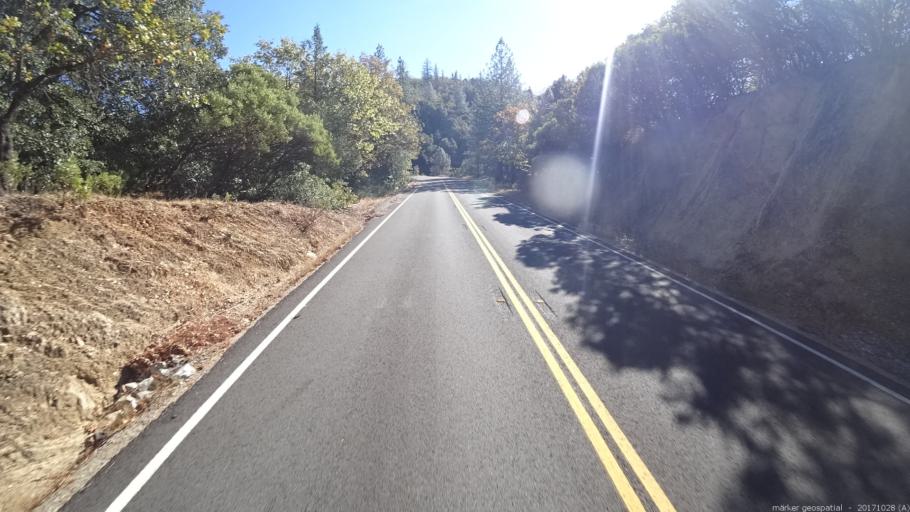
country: US
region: California
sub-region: Shasta County
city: Shasta
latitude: 40.6104
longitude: -122.5650
